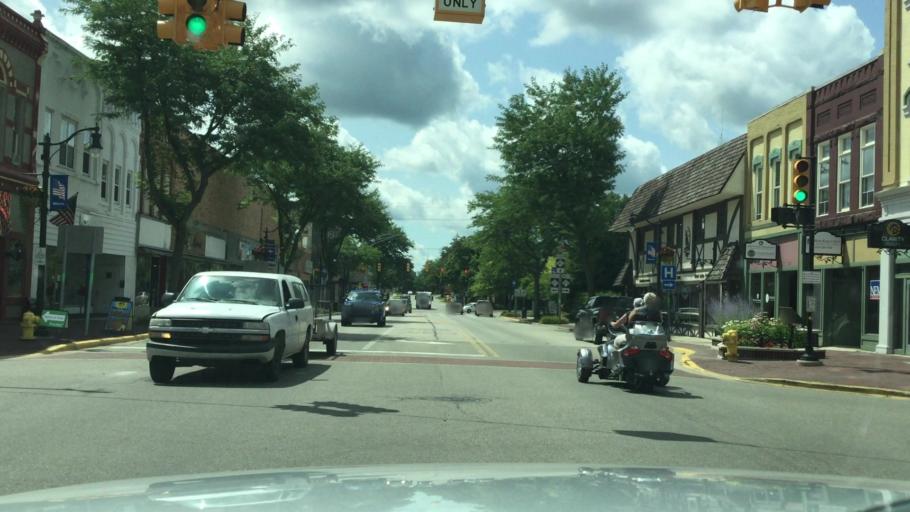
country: US
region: Michigan
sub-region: Montcalm County
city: Greenville
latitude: 43.1787
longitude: -85.2532
